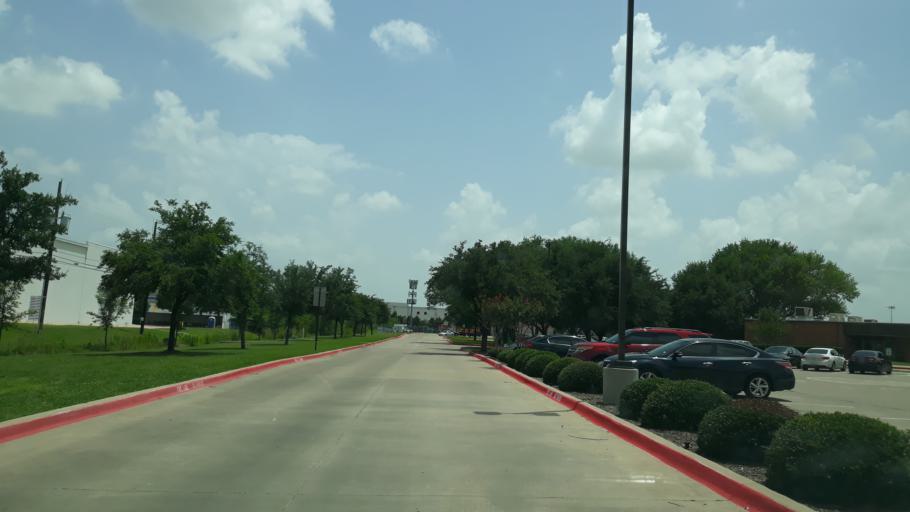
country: US
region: Texas
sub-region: Dallas County
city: Coppell
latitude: 32.9379
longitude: -97.0016
